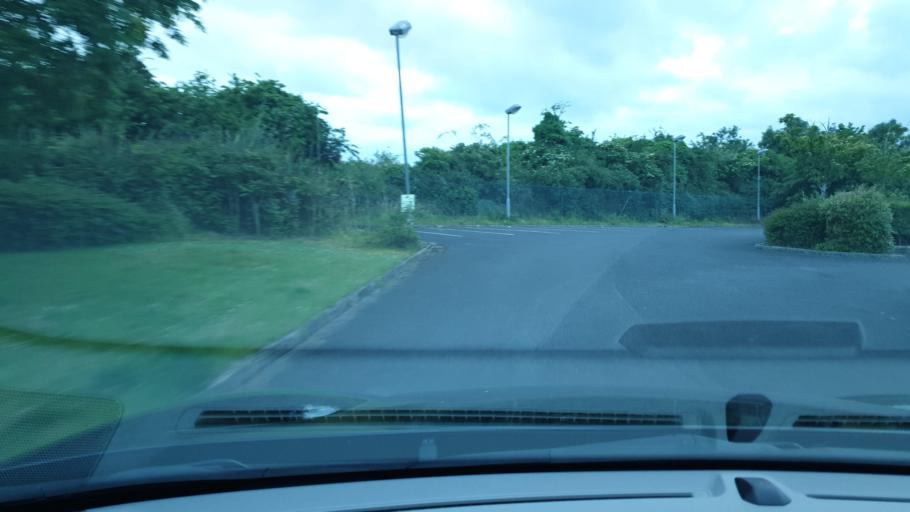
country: IE
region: Leinster
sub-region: Fingal County
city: Swords
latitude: 53.4505
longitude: -6.2197
